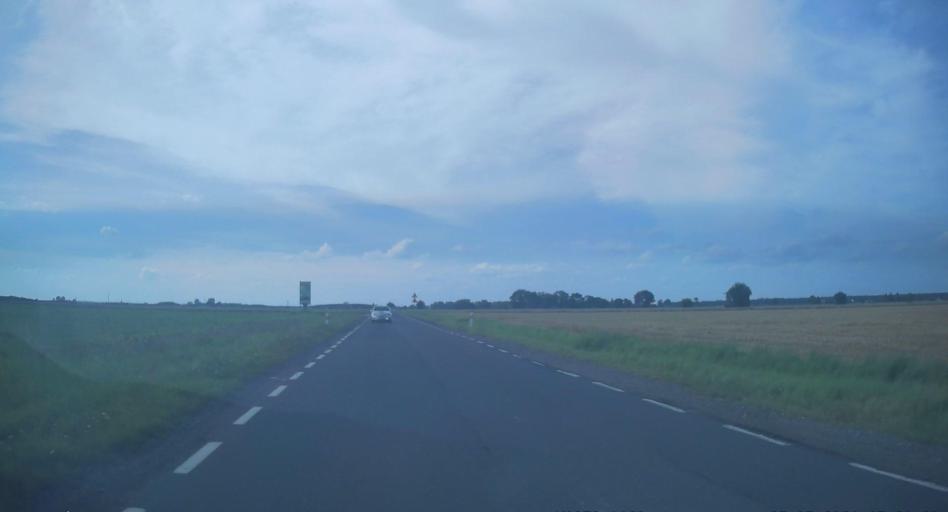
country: PL
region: Lodz Voivodeship
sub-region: Powiat tomaszowski
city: Rzeczyca
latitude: 51.6654
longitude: 20.2657
